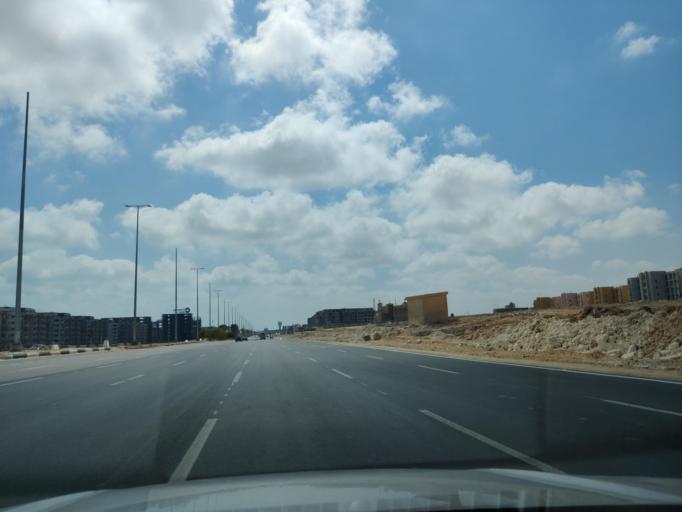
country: EG
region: Muhafazat Matruh
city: Al `Alamayn
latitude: 30.8464
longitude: 28.9256
